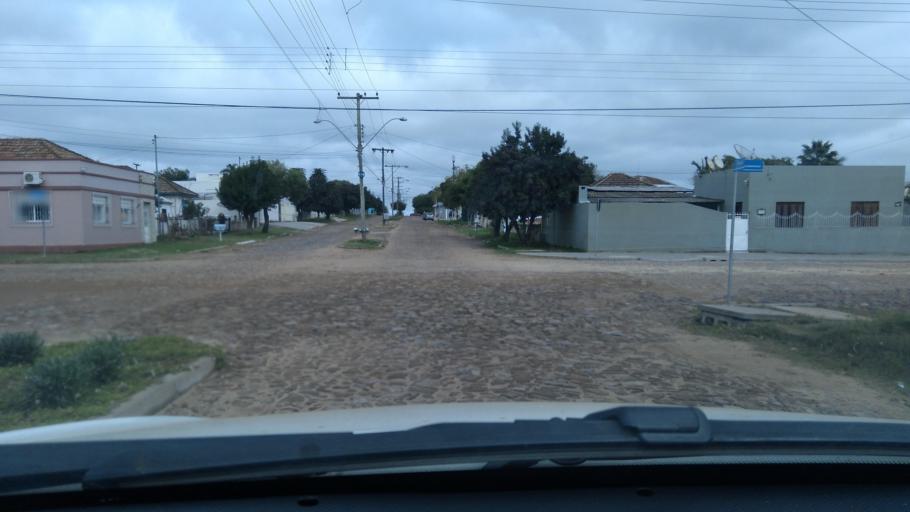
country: BR
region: Rio Grande do Sul
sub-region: Dom Pedrito
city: Dom Pedrito
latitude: -30.9843
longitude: -54.6630
